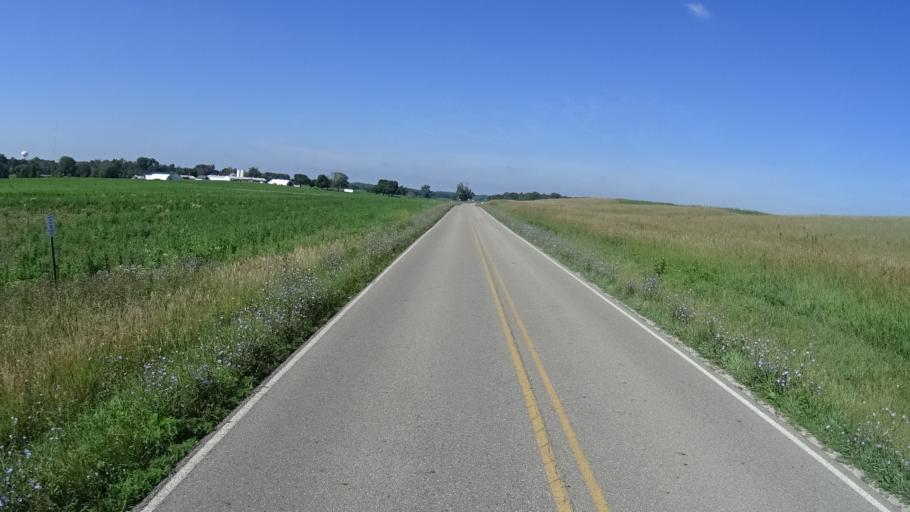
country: US
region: Indiana
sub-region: Madison County
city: Pendleton
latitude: 39.9913
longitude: -85.7657
